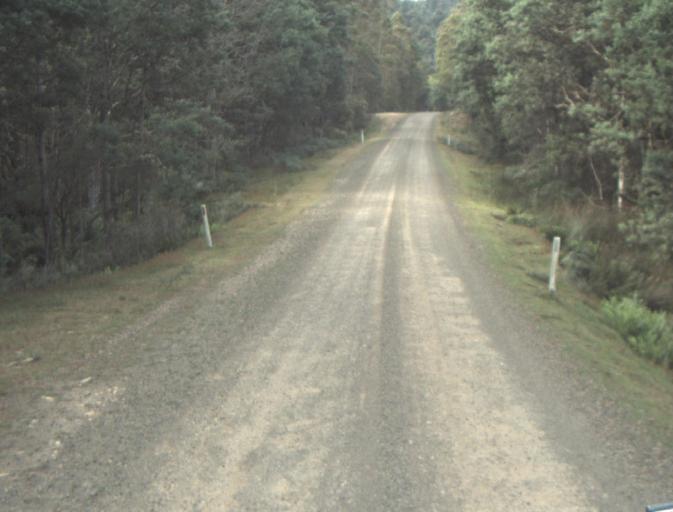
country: AU
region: Tasmania
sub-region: Dorset
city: Scottsdale
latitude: -41.3766
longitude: 147.4774
